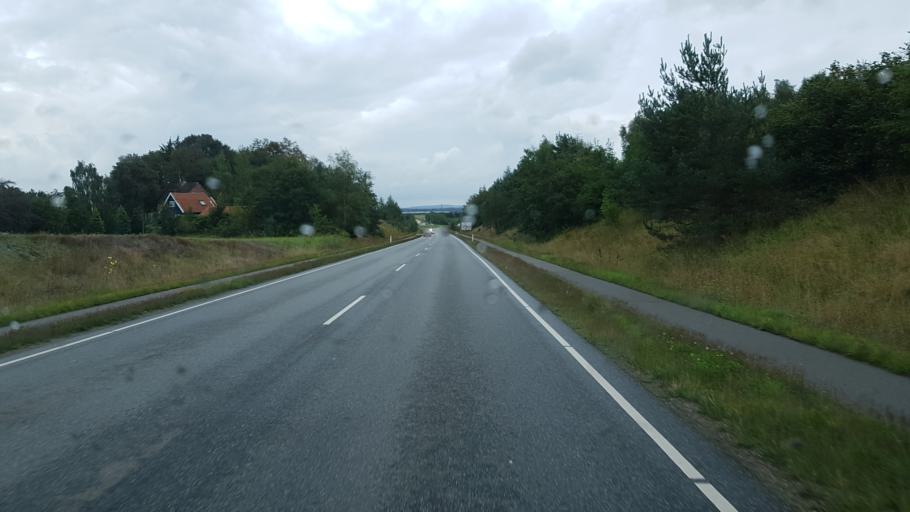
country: DK
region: Central Jutland
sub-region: Horsens Kommune
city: Horsens
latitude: 55.9006
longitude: 9.7479
